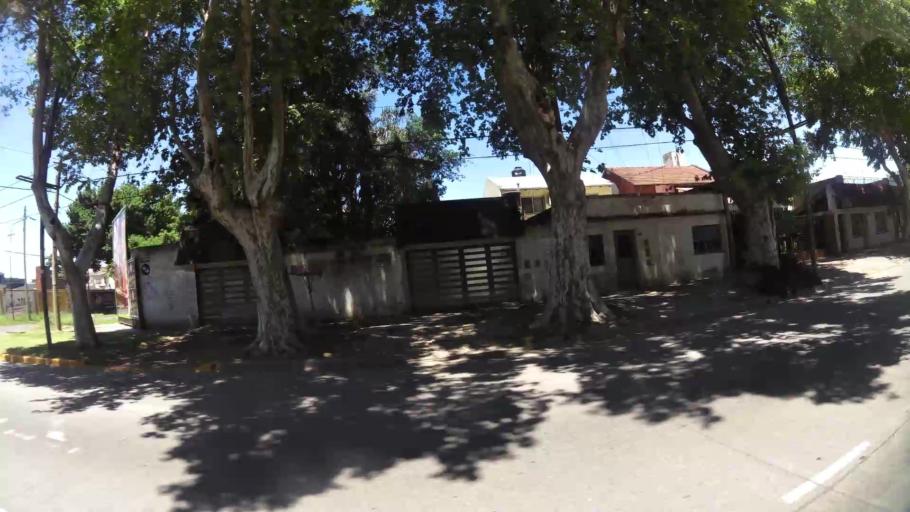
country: AR
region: Santa Fe
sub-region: Departamento de Rosario
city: Rosario
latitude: -32.9483
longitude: -60.6997
